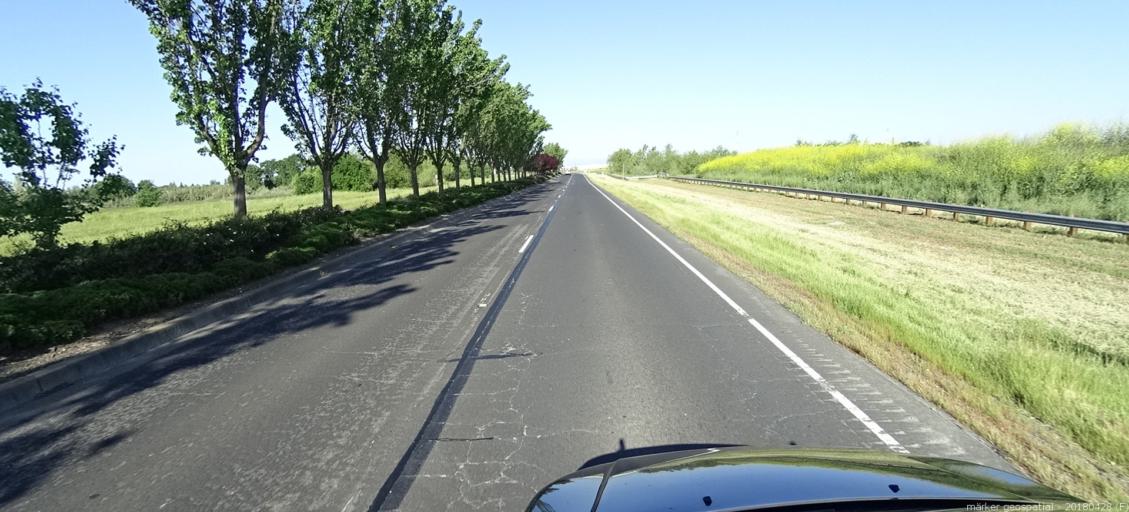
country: US
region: California
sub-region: Yolo County
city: West Sacramento
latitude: 38.5566
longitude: -121.5456
